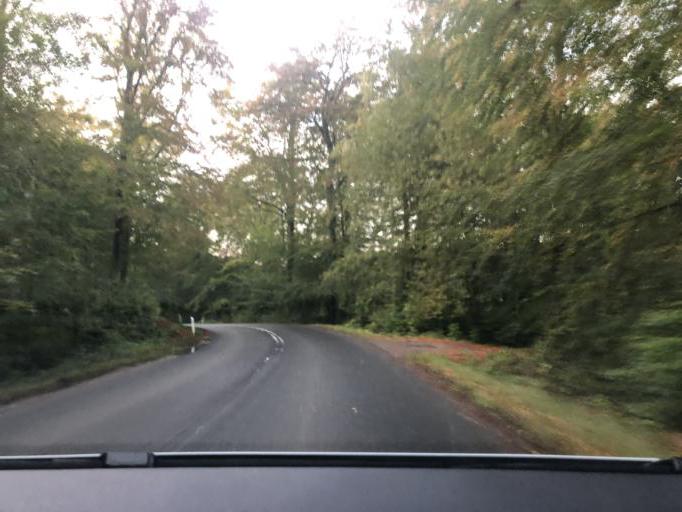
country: DK
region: Capital Region
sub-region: Egedal Kommune
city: Stenlose
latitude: 55.8114
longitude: 12.2087
